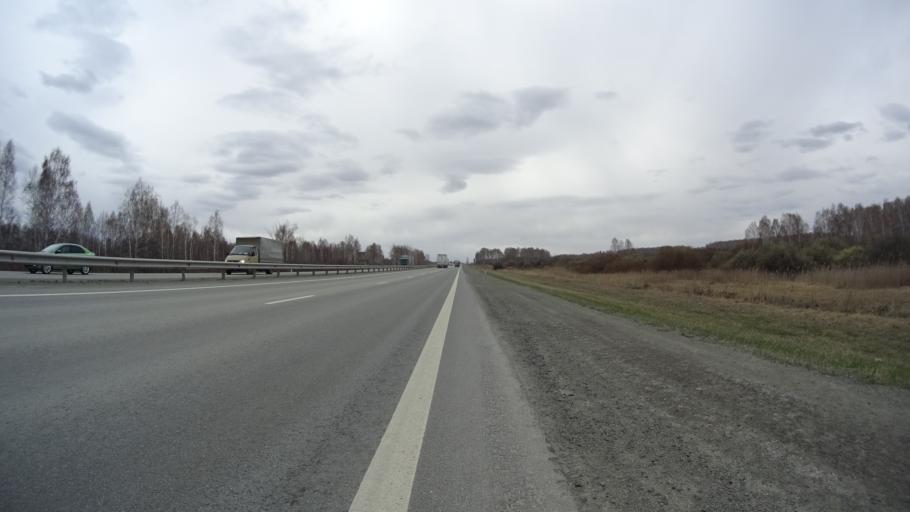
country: RU
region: Chelyabinsk
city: Yemanzhelinka
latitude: 54.8403
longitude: 61.3134
